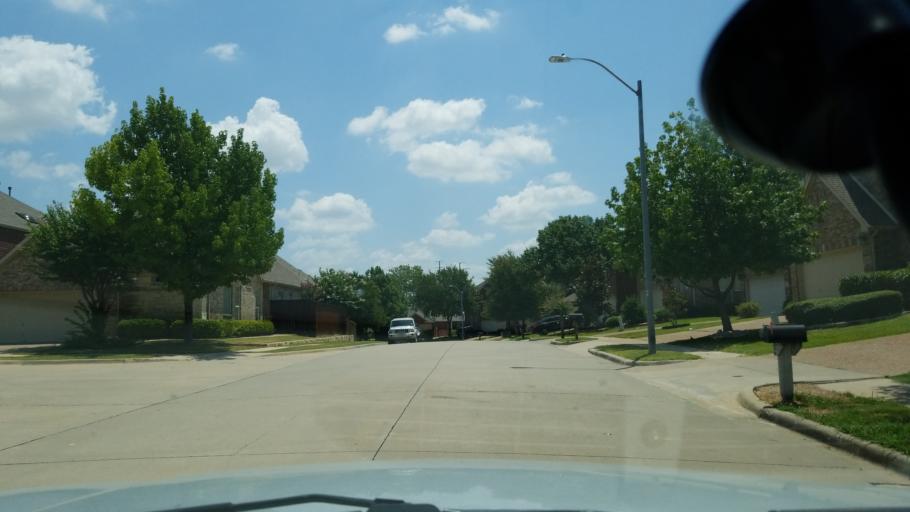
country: US
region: Texas
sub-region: Dallas County
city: Farmers Branch
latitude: 32.9177
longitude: -96.9502
